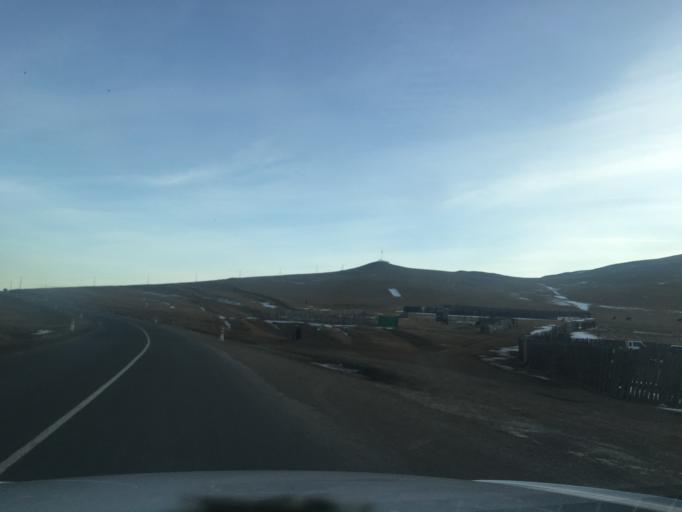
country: MN
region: Central Aimak
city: Mandal
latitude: 48.1999
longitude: 106.7057
